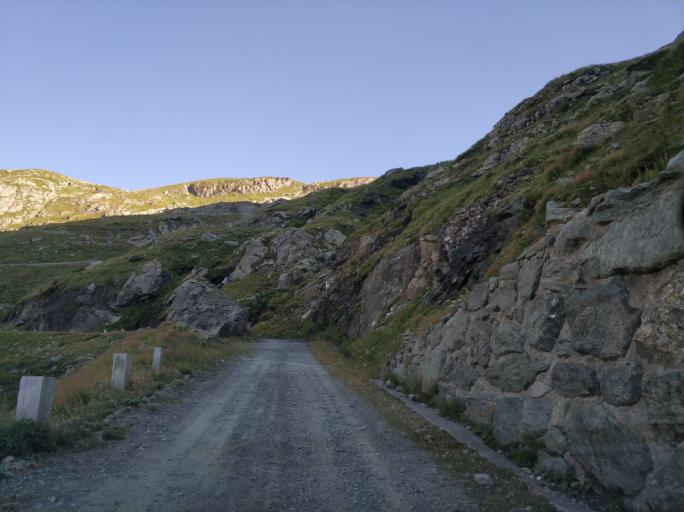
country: IT
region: Piedmont
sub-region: Provincia di Torino
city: Usseglio
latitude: 45.2551
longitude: 7.1812
